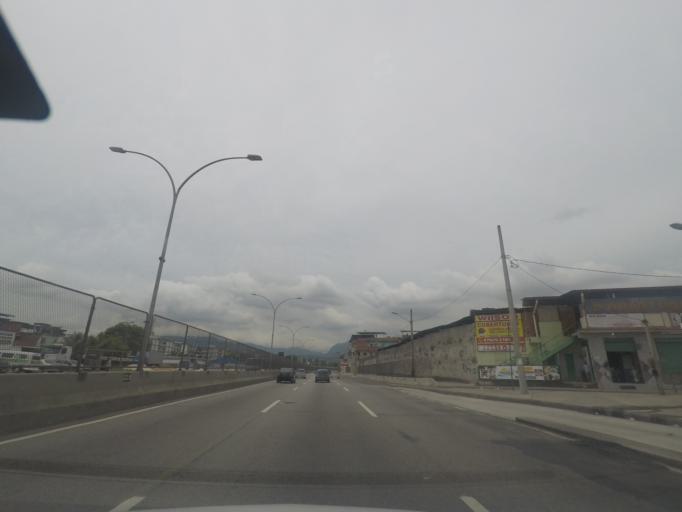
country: BR
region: Rio de Janeiro
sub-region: Rio De Janeiro
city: Rio de Janeiro
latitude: -22.8641
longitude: -43.2393
